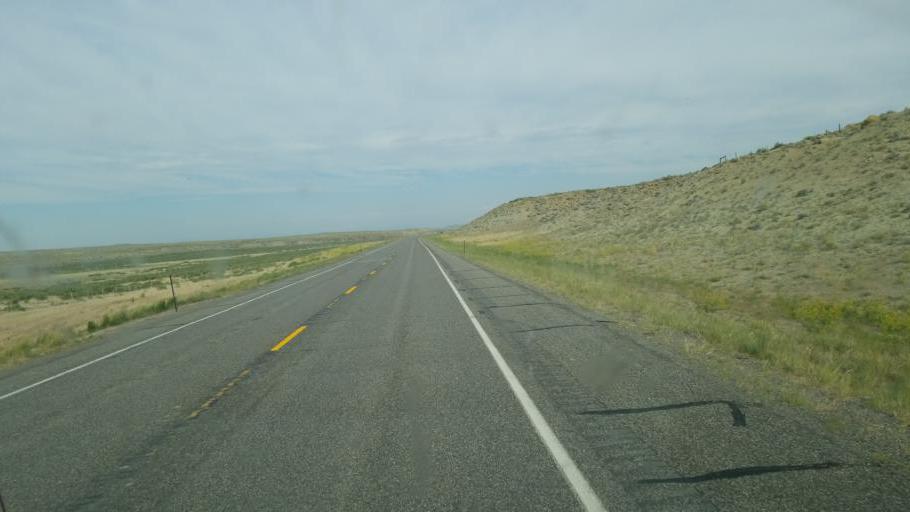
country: US
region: Wyoming
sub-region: Fremont County
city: Riverton
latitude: 43.2234
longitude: -108.0359
